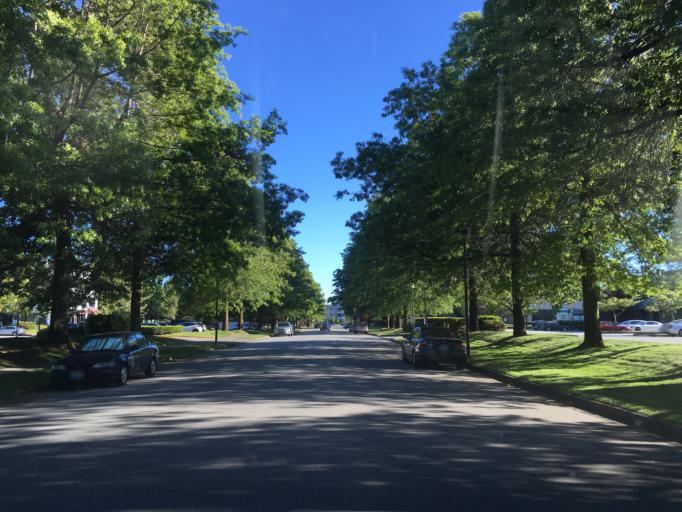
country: CA
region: British Columbia
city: Richmond
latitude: 49.1752
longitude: -123.0717
